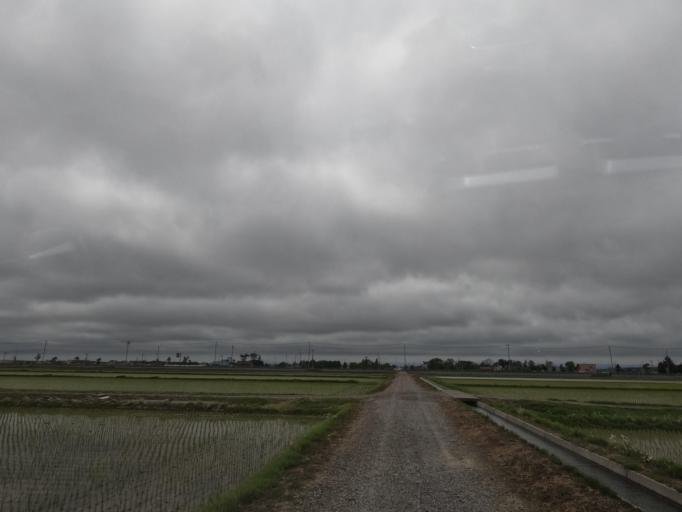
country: JP
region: Hokkaido
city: Tobetsu
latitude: 43.2457
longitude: 141.5191
